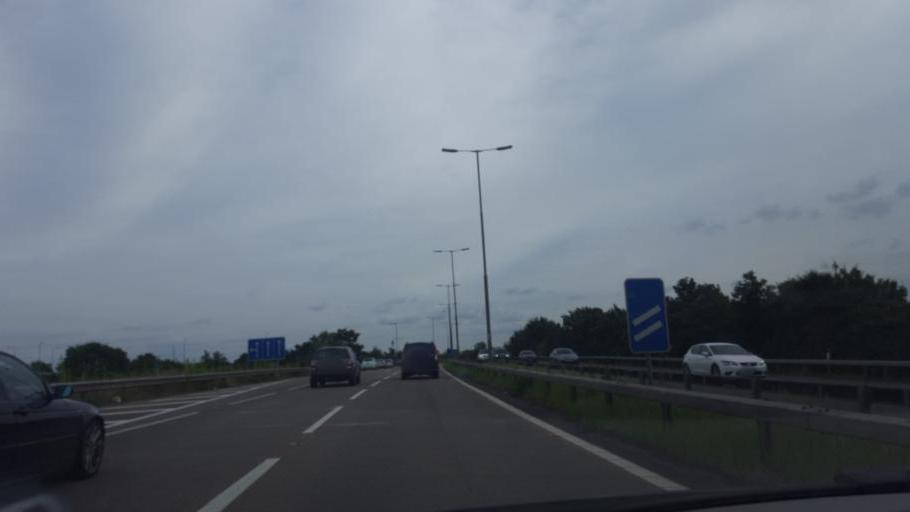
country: GB
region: England
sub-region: Royal Borough of Windsor and Maidenhead
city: Maidenhead
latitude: 51.5016
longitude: -0.7260
